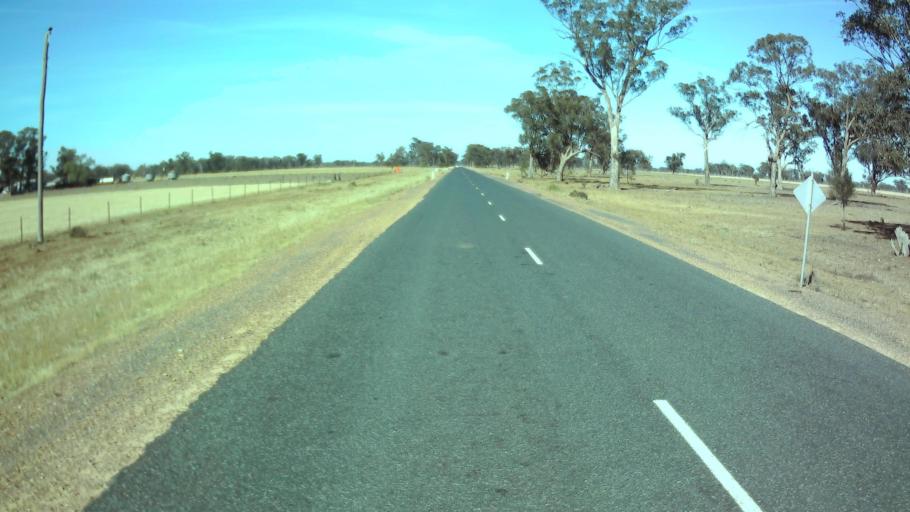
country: AU
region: New South Wales
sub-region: Weddin
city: Grenfell
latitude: -34.0983
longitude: 147.8821
